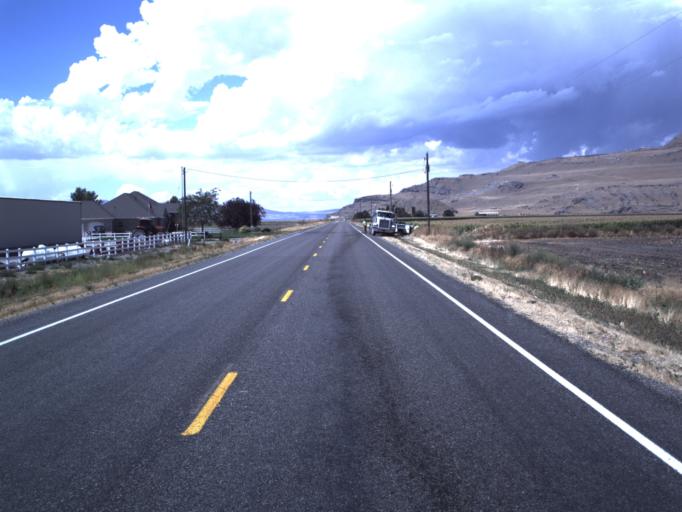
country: US
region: Utah
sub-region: Box Elder County
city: Elwood
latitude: 41.5712
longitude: -112.2069
